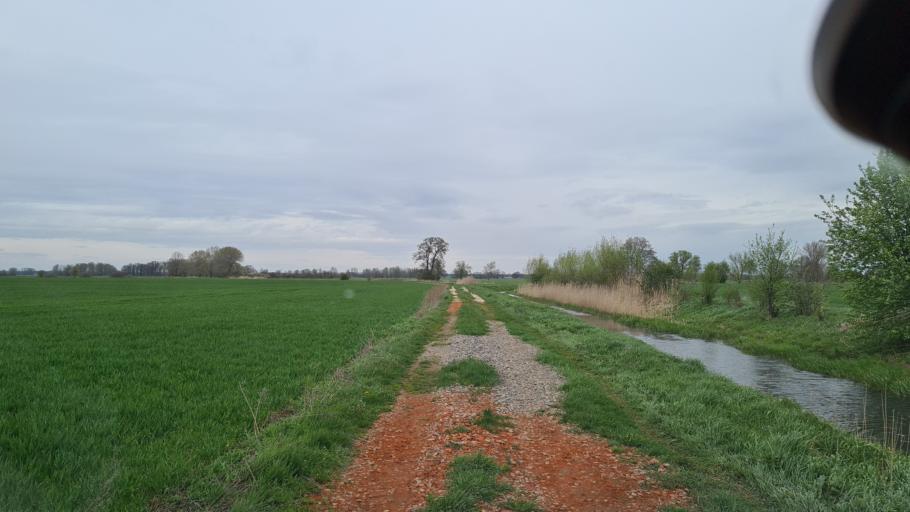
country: DE
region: Brandenburg
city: Doberlug-Kirchhain
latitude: 51.6618
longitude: 13.5658
